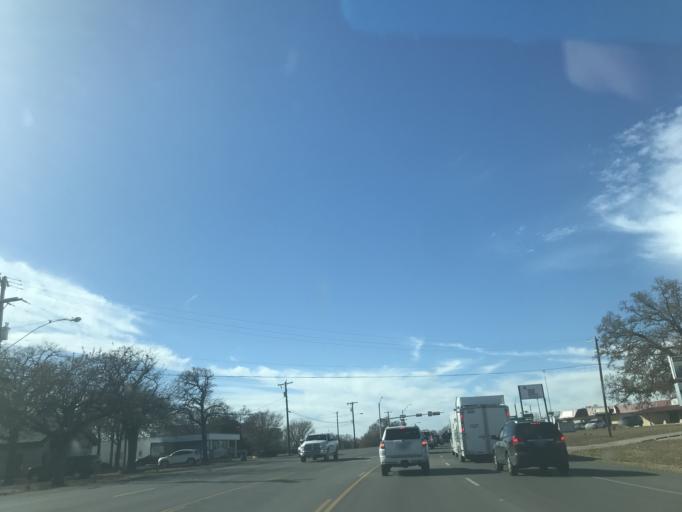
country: US
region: Texas
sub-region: Erath County
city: Stephenville
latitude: 32.2045
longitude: -98.2135
